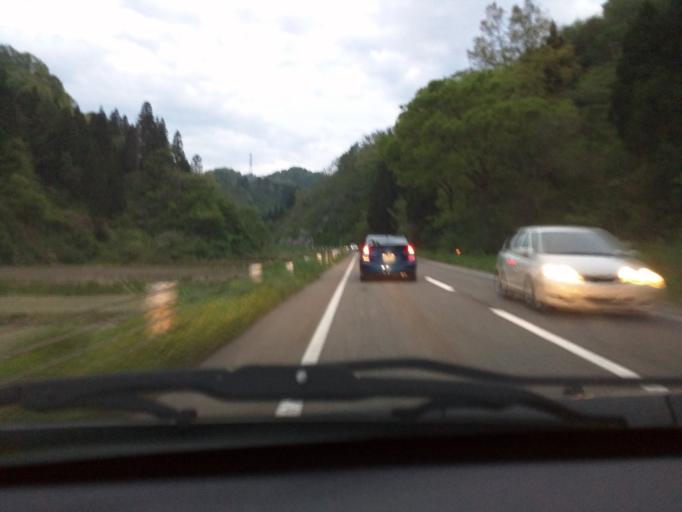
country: JP
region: Niigata
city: Ojiya
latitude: 37.3234
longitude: 138.6811
